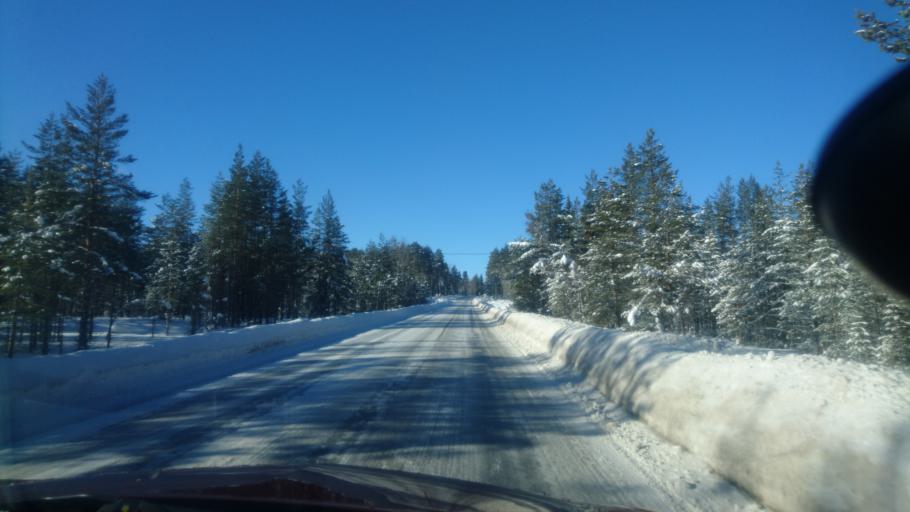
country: NO
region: Hedmark
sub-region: Trysil
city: Innbygda
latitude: 61.2511
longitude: 12.5447
